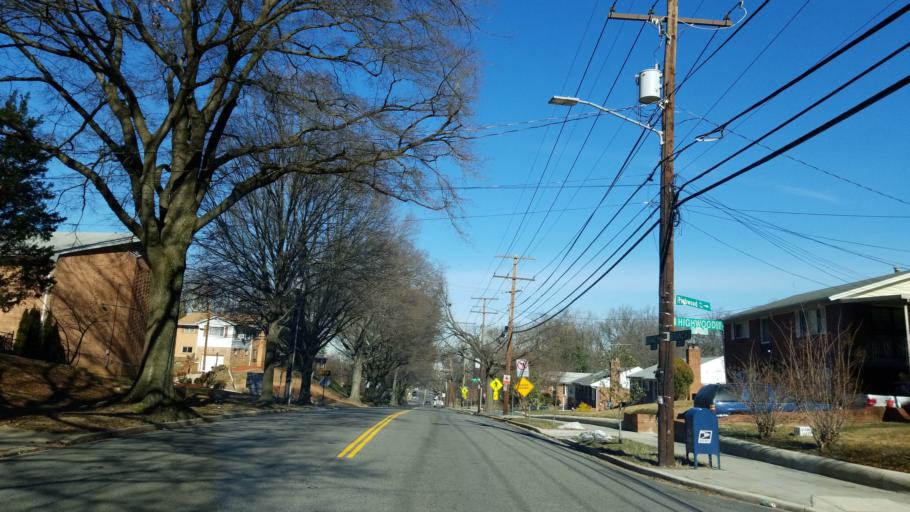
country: US
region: Maryland
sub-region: Prince George's County
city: Silver Hill
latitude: 38.8732
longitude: -76.9608
